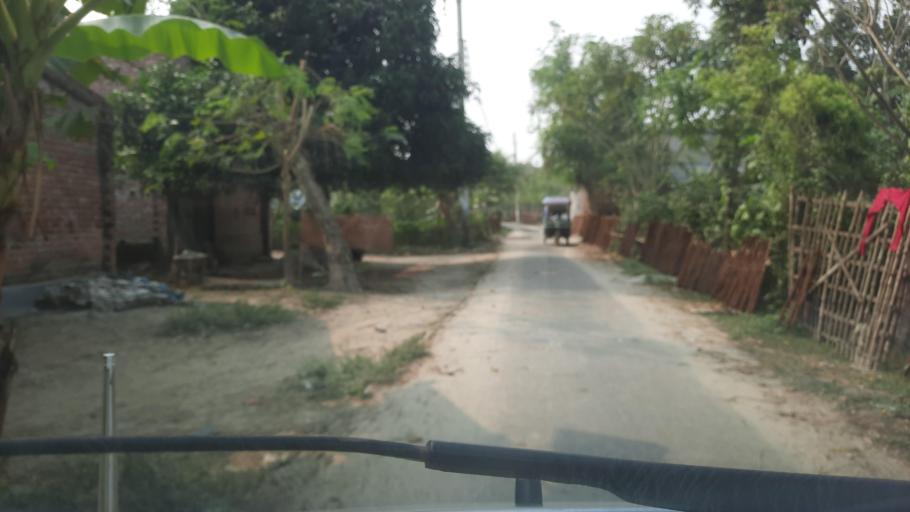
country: BD
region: Khulna
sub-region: Chuadanga
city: Nowlamary
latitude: 23.6442
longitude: 88.8873
